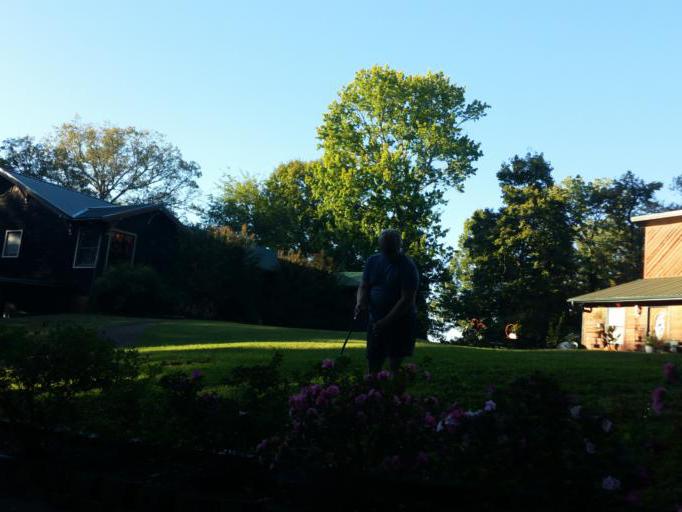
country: US
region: Tennessee
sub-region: Knox County
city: Knoxville
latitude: 35.9266
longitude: -83.9512
